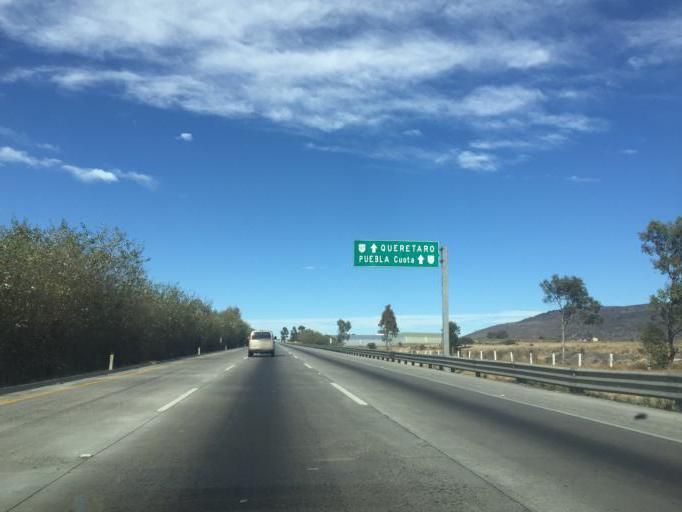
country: MX
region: Mexico
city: San Francisco Soyaniquilpan
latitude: 19.9902
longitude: -99.4606
